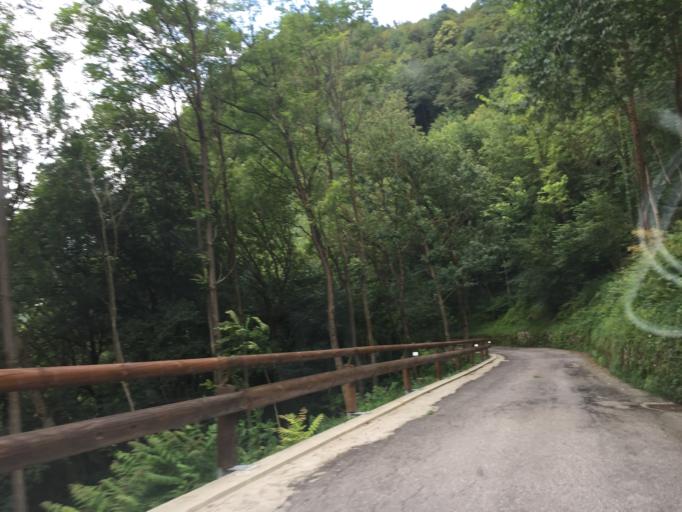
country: IT
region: Veneto
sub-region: Provincia di Belluno
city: Feltre
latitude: 46.0027
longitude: 11.9394
